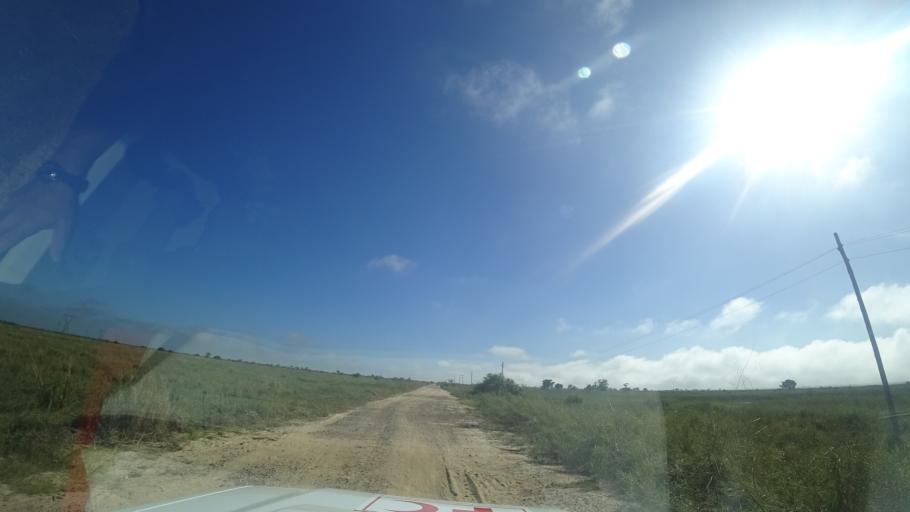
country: MZ
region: Sofala
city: Dondo
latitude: -19.4581
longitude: 34.5631
